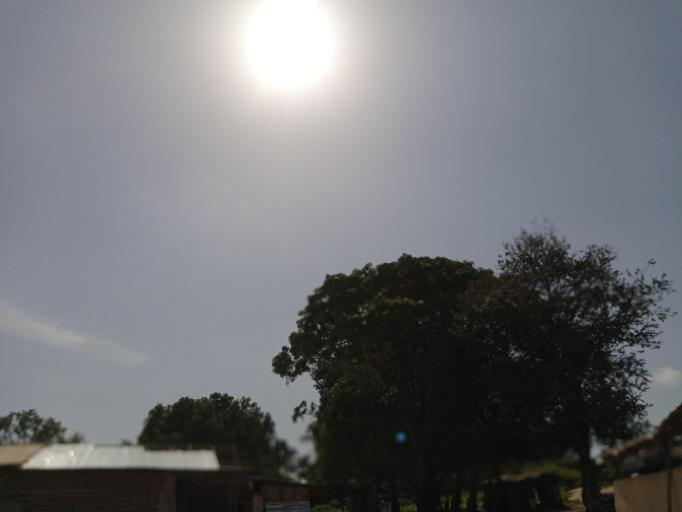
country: SL
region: Northern Province
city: Masoyila
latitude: 8.6128
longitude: -13.2021
